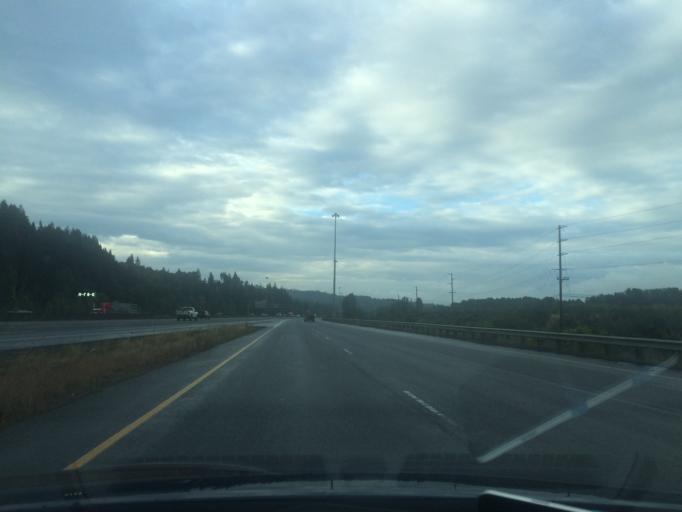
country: US
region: Washington
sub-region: Cowlitz County
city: Kelso
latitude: 46.1041
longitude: -122.8779
